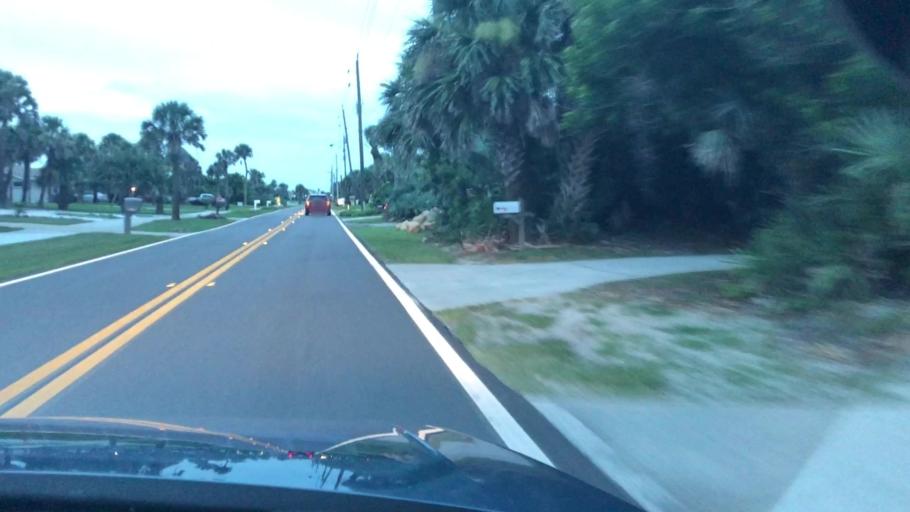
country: US
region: Florida
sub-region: Volusia County
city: Ponce Inlet
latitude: 29.1196
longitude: -80.9509
